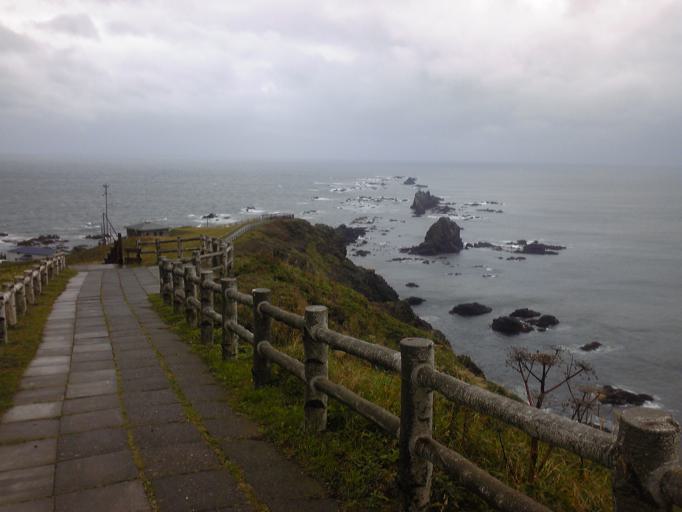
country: JP
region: Hokkaido
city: Shizunai-furukawacho
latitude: 41.9260
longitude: 143.2454
